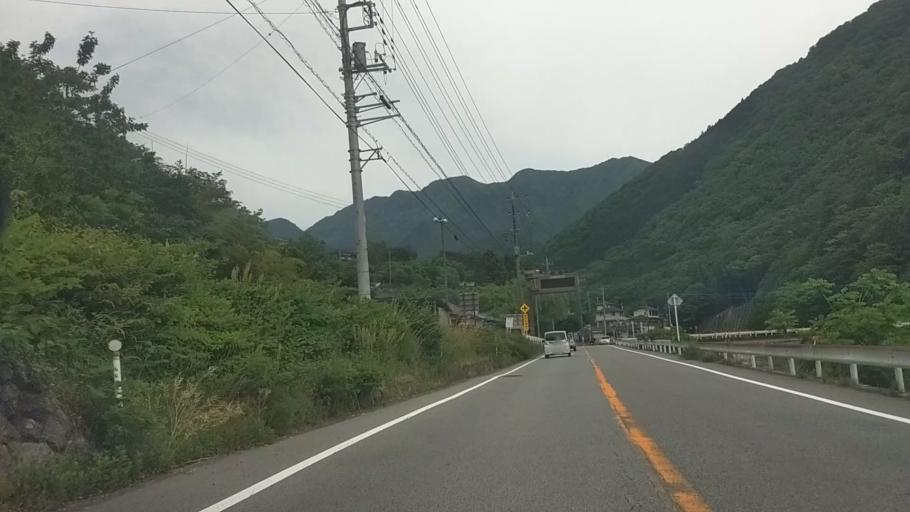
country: JP
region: Yamanashi
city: Fujikawaguchiko
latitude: 35.5334
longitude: 138.6055
